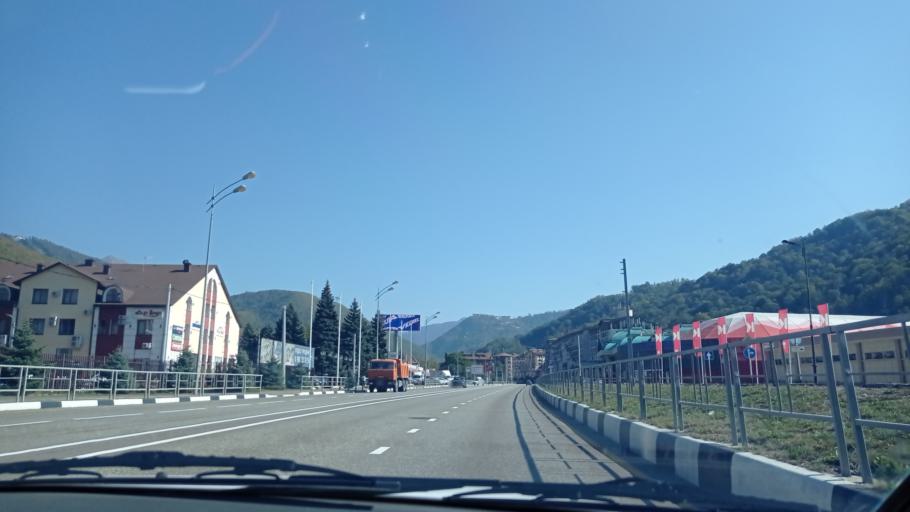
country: RU
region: Krasnodarskiy
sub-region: Sochi City
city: Krasnaya Polyana
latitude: 43.6863
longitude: 40.2518
